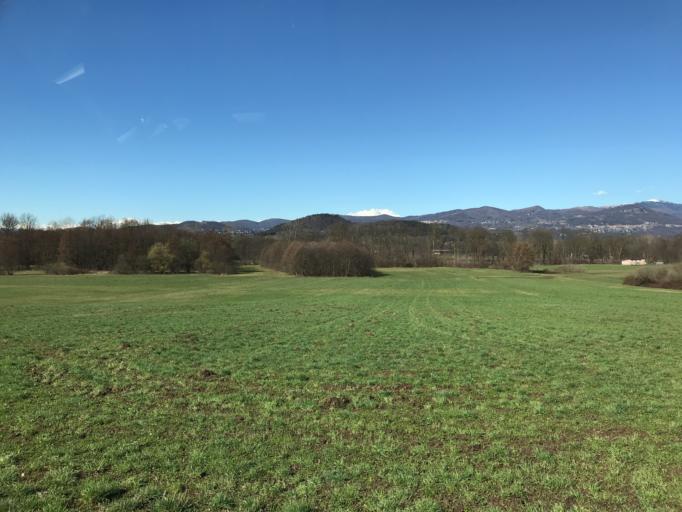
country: IT
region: Lombardy
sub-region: Provincia di Varese
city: Taino
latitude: 45.7799
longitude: 8.6156
